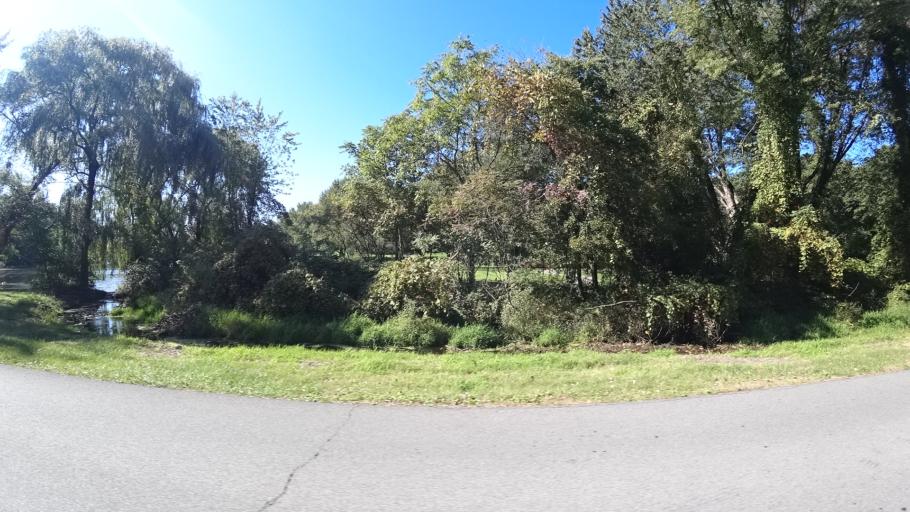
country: US
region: Indiana
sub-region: LaPorte County
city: Long Beach
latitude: 41.7465
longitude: -86.8364
